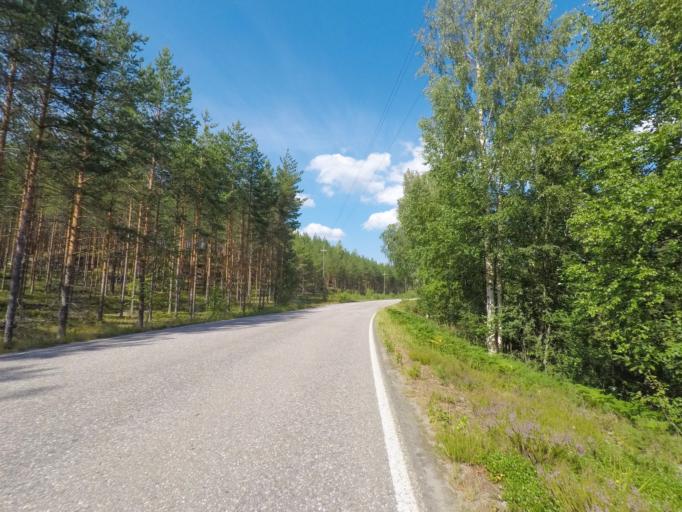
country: FI
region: Southern Savonia
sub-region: Mikkeli
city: Puumala
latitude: 61.4749
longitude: 28.1691
